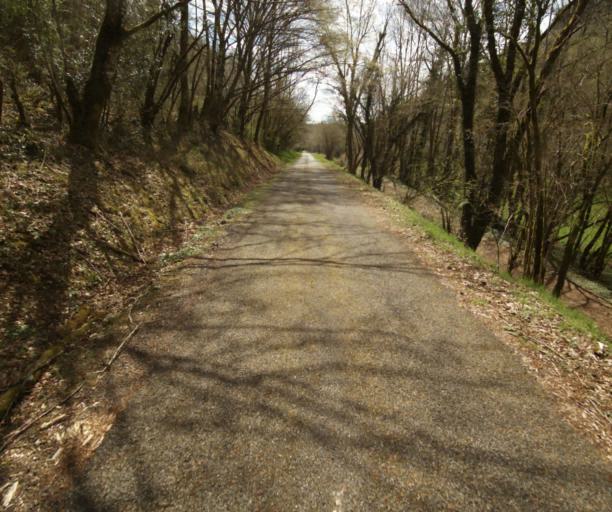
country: FR
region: Limousin
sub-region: Departement de la Correze
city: Argentat
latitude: 45.1820
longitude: 1.8766
